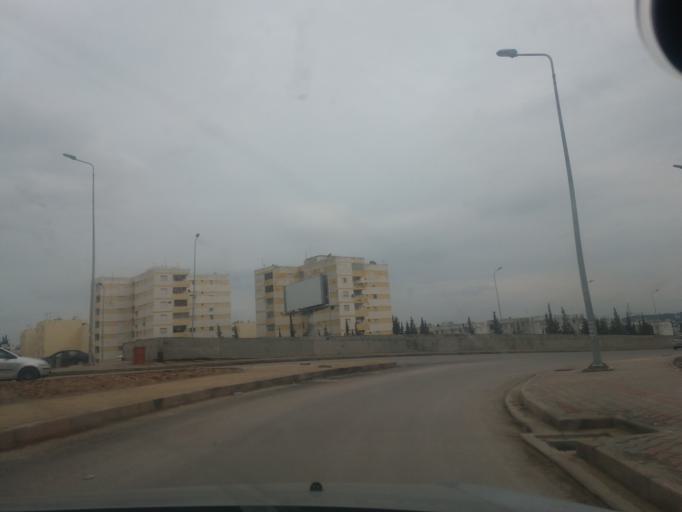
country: TN
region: Tunis
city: Tunis
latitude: 36.8548
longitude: 10.1522
